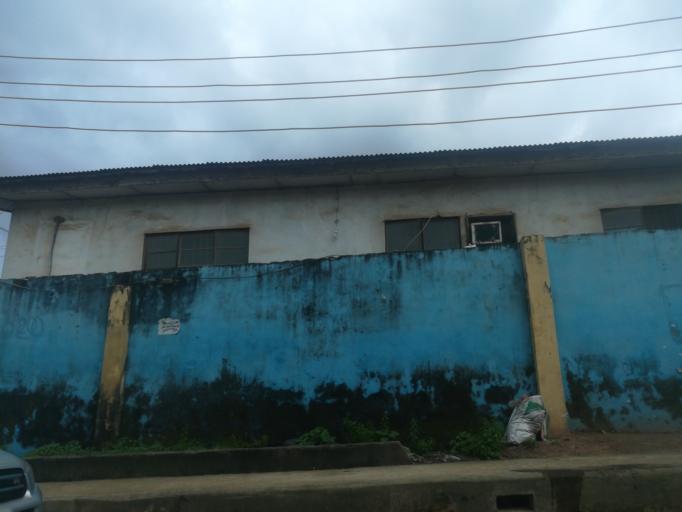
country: NG
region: Lagos
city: Ojota
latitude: 6.5641
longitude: 3.3846
